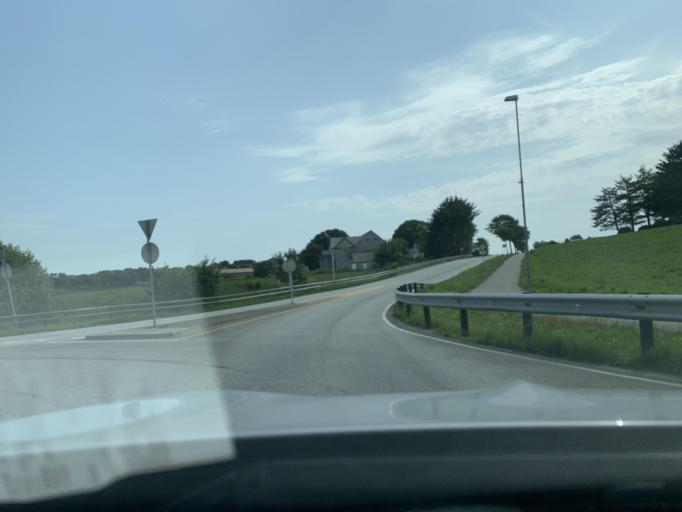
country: NO
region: Rogaland
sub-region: Klepp
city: Kleppe
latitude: 58.7672
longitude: 5.6282
